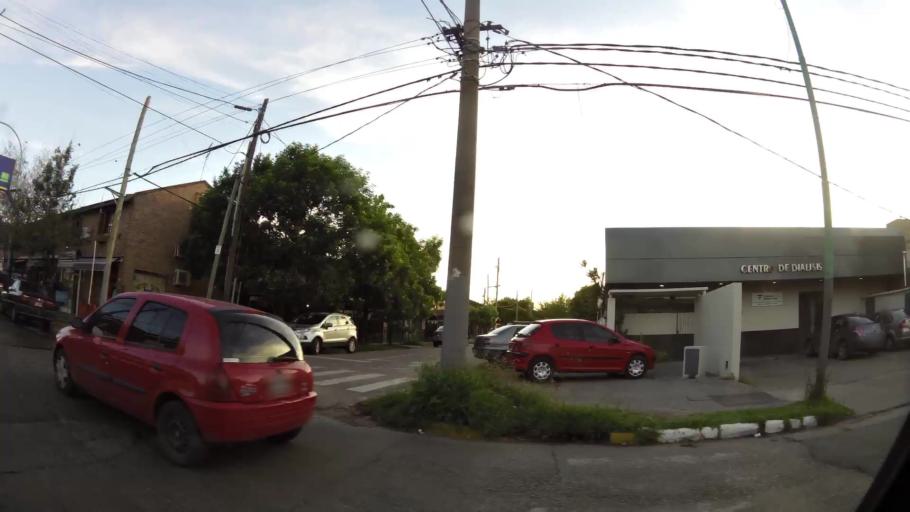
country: AR
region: Buenos Aires
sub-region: Partido de Quilmes
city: Quilmes
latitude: -34.7811
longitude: -58.2107
